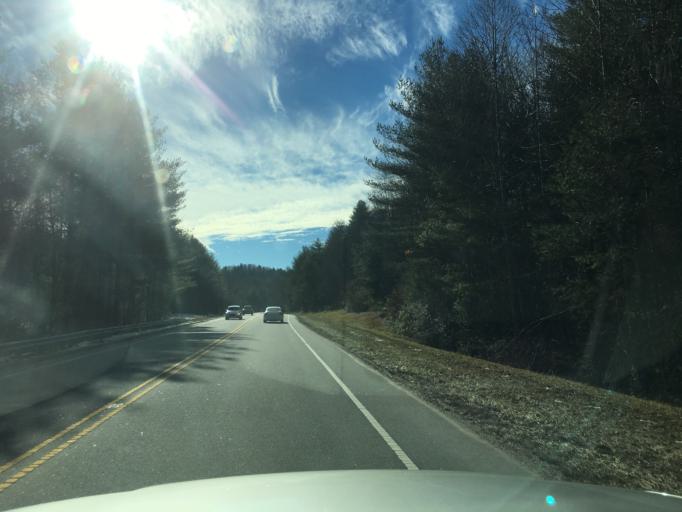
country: US
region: North Carolina
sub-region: Transylvania County
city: Brevard
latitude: 35.1884
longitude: -82.7890
